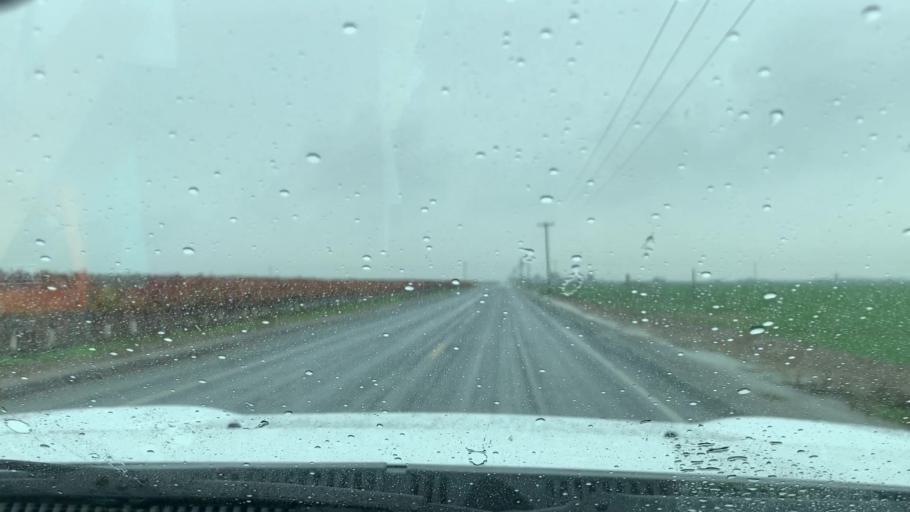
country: US
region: California
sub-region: Tulare County
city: Earlimart
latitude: 35.8919
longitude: -119.2997
